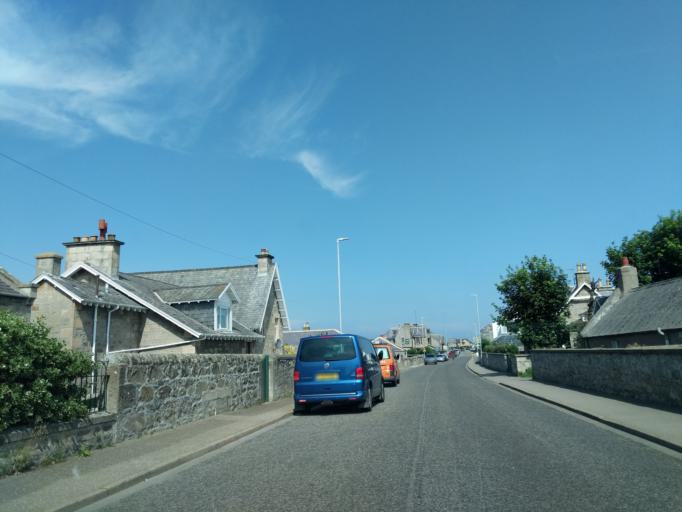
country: GB
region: Scotland
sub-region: Moray
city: Lossiemouth
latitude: 57.7192
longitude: -3.2990
